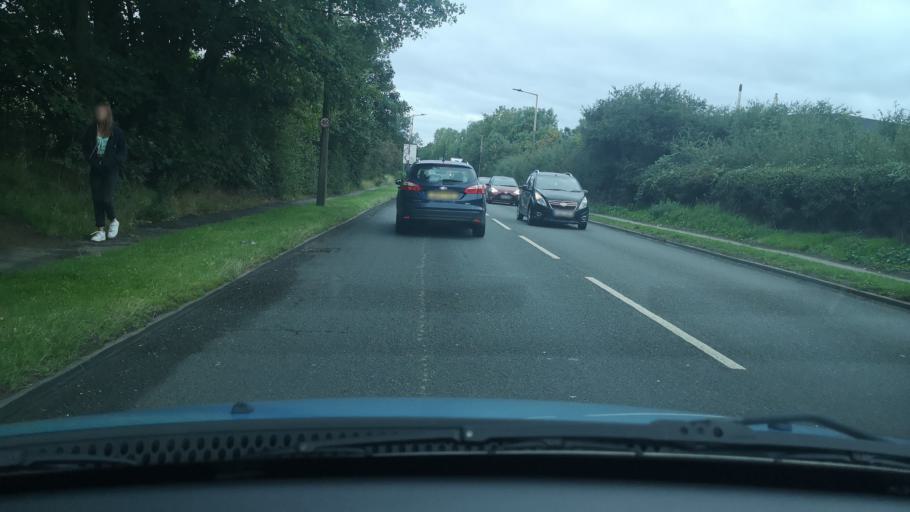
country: GB
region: England
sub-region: Doncaster
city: Kirk Sandall
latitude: 53.5555
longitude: -1.0797
